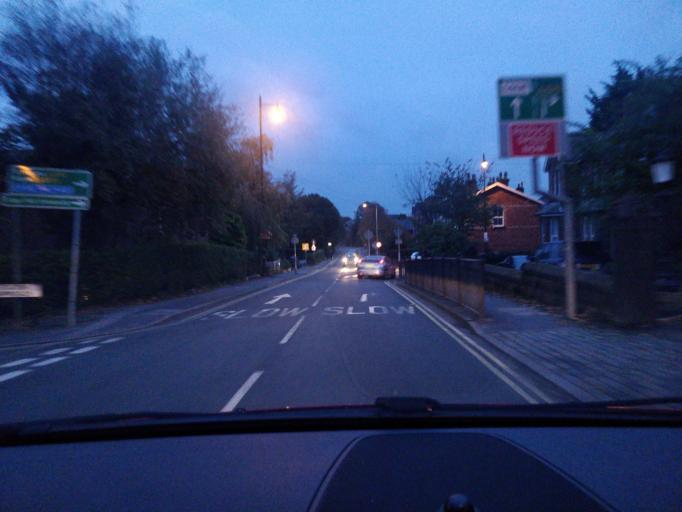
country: GB
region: England
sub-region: Lancashire
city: Ormskirk
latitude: 53.5684
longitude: -2.8818
